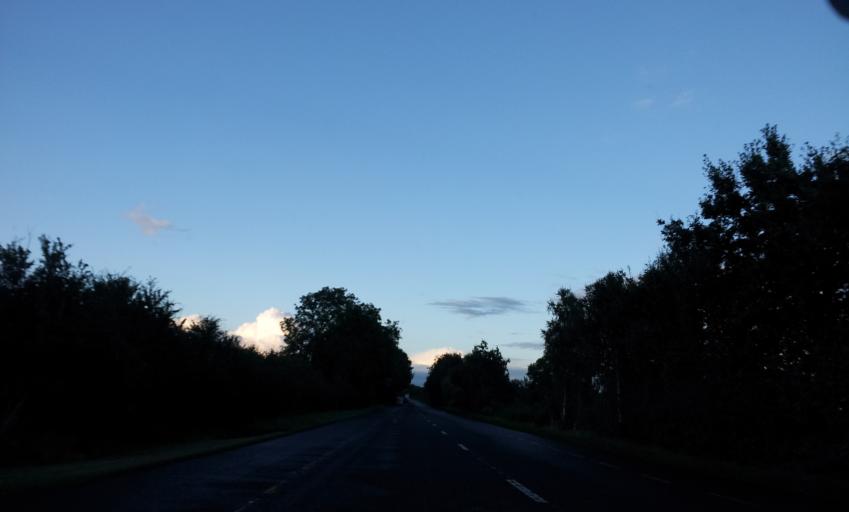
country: IE
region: Munster
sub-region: County Limerick
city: Rathkeale
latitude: 52.4929
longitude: -8.9999
